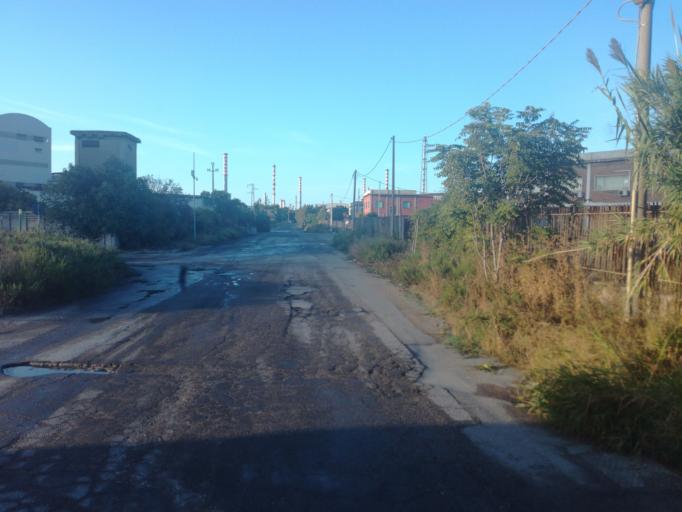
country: IT
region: Apulia
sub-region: Provincia di Taranto
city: Statte
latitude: 40.5018
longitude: 17.1992
